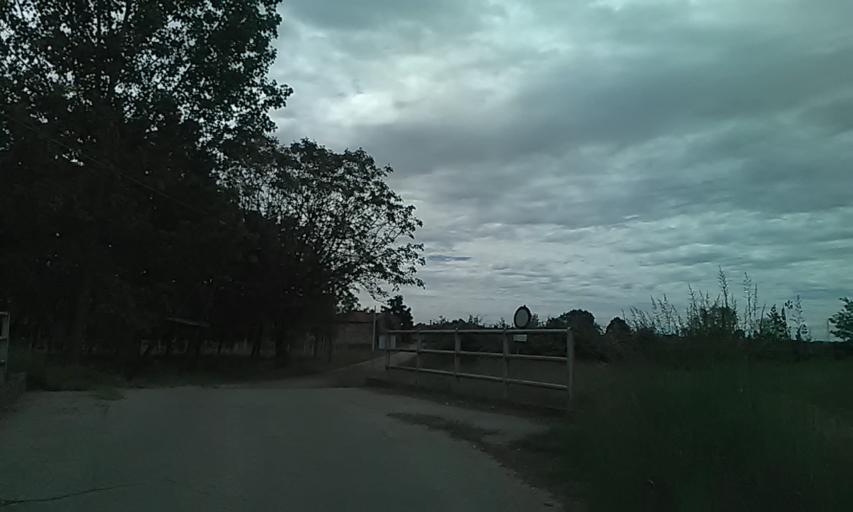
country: IT
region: Piedmont
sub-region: Provincia di Vercelli
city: Borgo d'Ale
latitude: 45.3220
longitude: 8.0496
